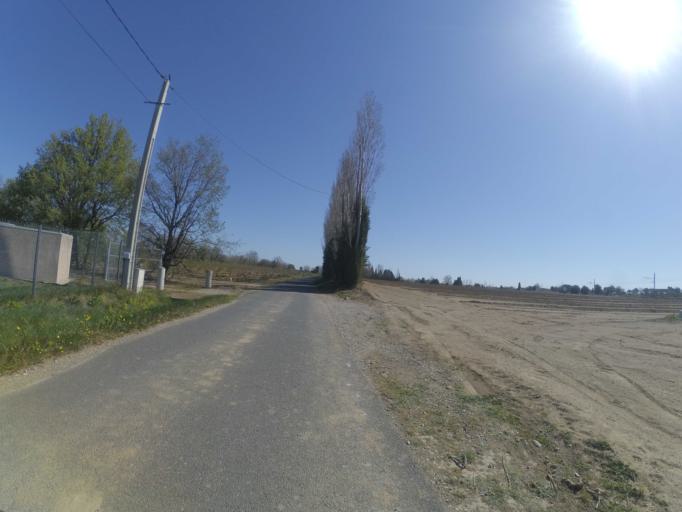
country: FR
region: Languedoc-Roussillon
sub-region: Departement des Pyrenees-Orientales
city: Millas
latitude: 42.6842
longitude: 2.7123
